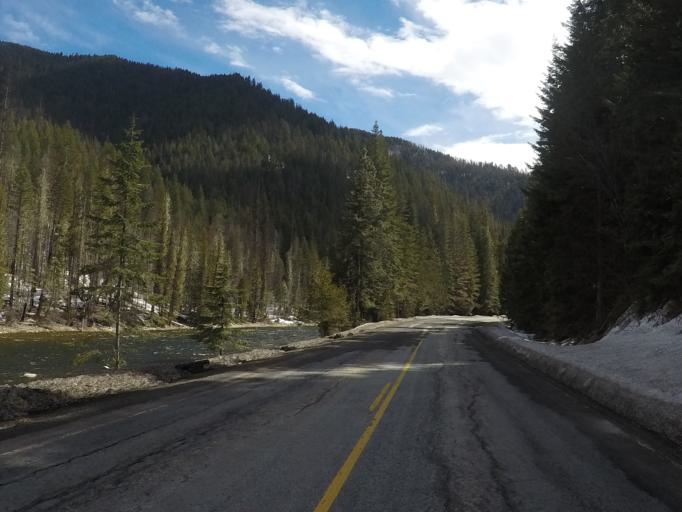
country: US
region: Montana
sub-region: Mineral County
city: Superior
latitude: 46.4793
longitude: -114.8753
